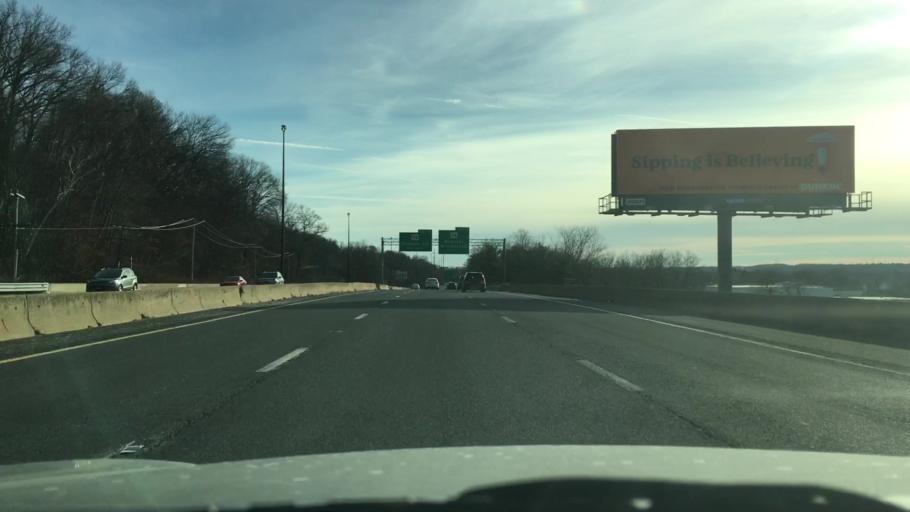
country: US
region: Massachusetts
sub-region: Hampden County
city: North Chicopee
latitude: 42.1722
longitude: -72.6102
